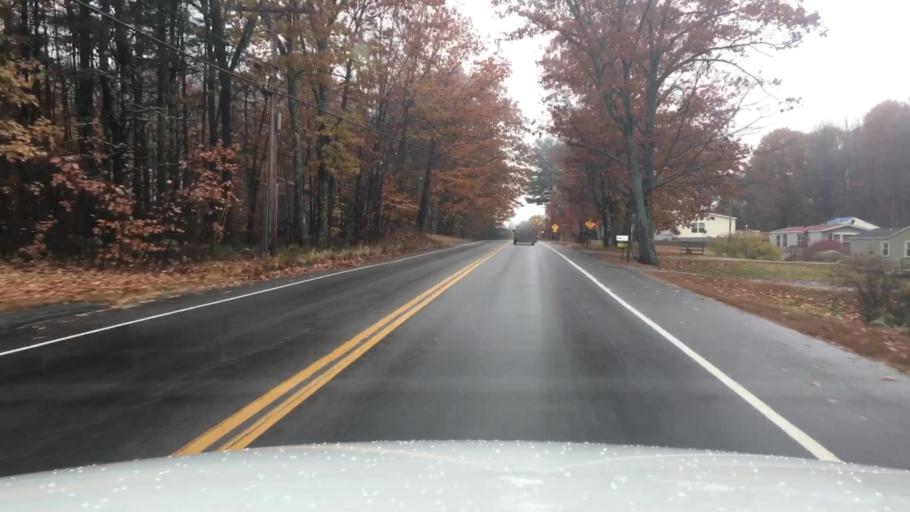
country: US
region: Maine
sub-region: Androscoggin County
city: Sabattus
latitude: 44.1134
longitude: -70.0980
